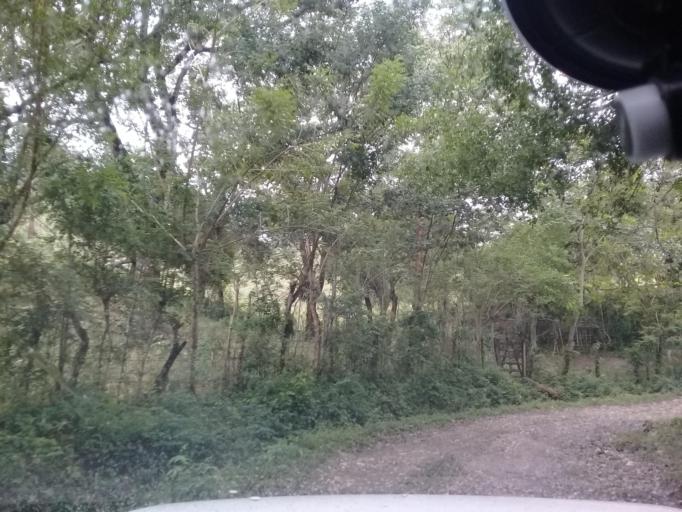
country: MX
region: Veracruz
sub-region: Chalma
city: San Pedro Coyutla
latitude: 21.2470
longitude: -98.4138
